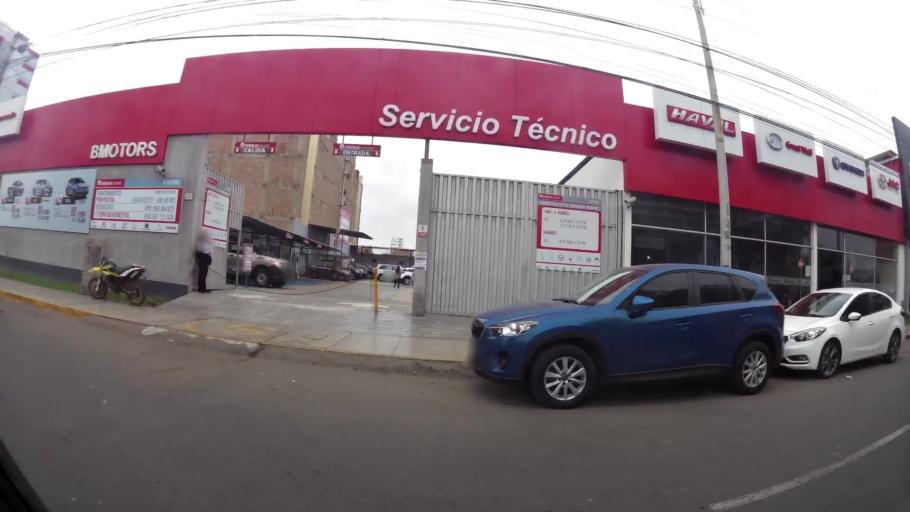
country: PE
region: La Libertad
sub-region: Provincia de Trujillo
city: Trujillo
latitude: -8.1213
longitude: -79.0277
